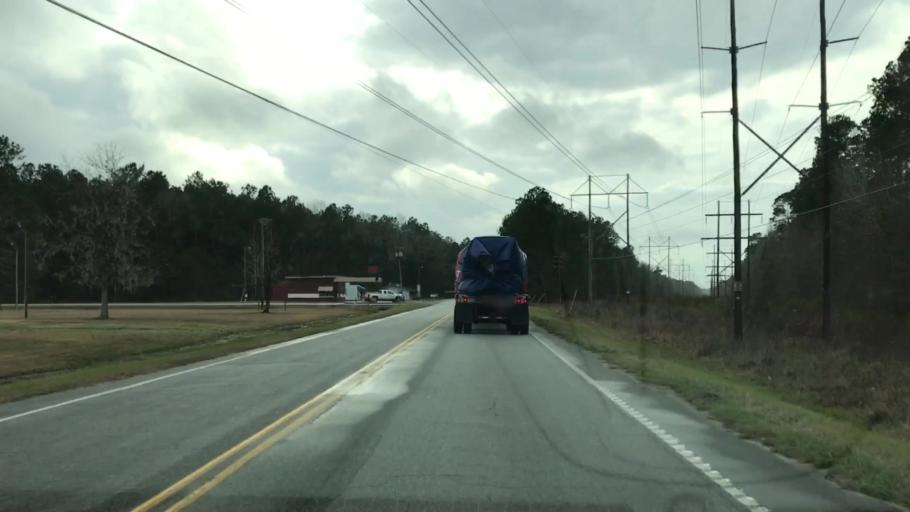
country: US
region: South Carolina
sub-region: Berkeley County
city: Bonneau Beach
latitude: 33.2713
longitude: -79.8977
